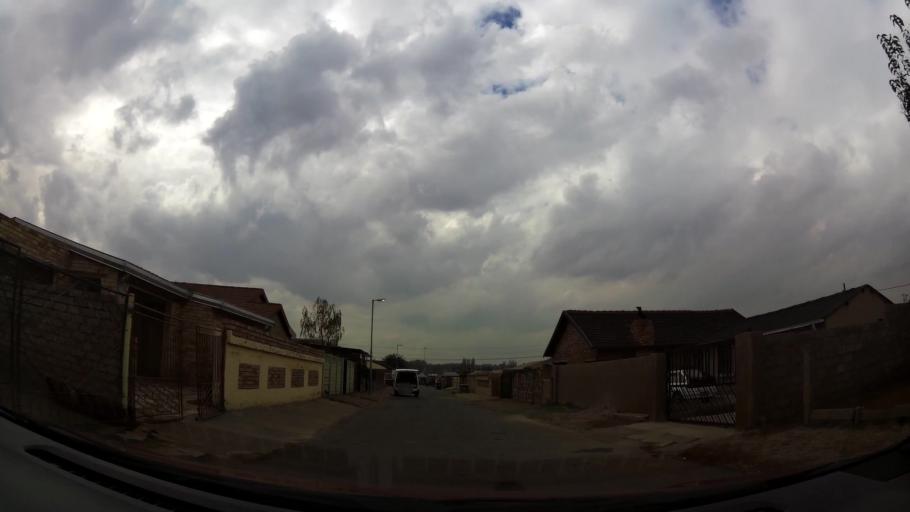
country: ZA
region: Gauteng
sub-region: City of Johannesburg Metropolitan Municipality
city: Soweto
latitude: -26.2633
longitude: 27.8363
